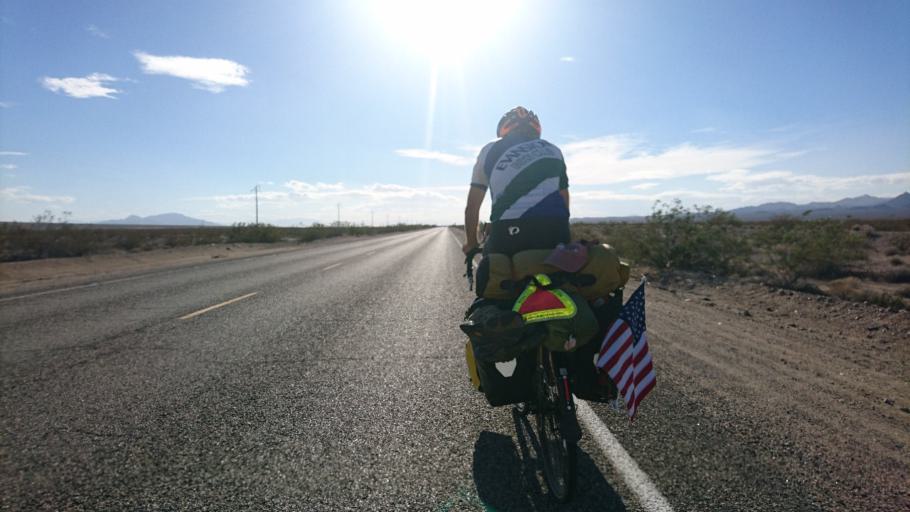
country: US
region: California
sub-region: San Bernardino County
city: Needles
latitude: 34.7141
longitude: -115.2788
